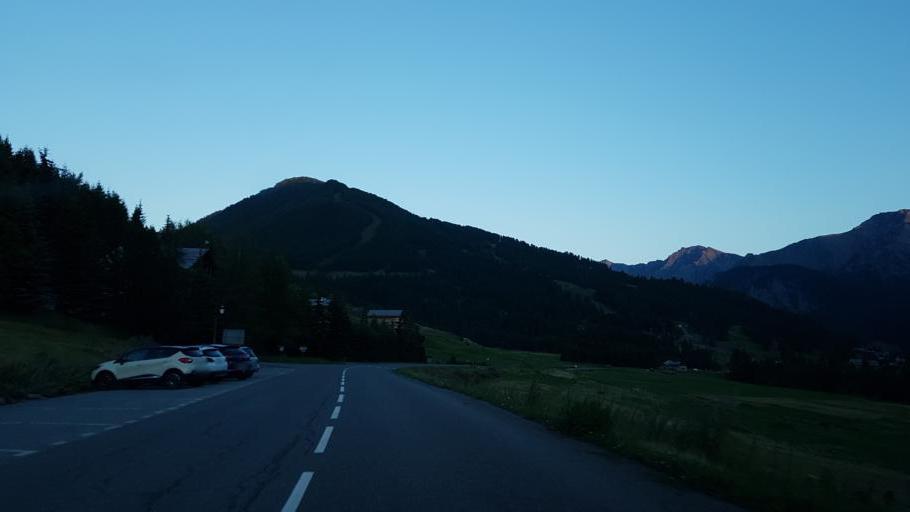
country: FR
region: Provence-Alpes-Cote d'Azur
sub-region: Departement des Hautes-Alpes
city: Guillestre
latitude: 44.7289
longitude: 6.8436
